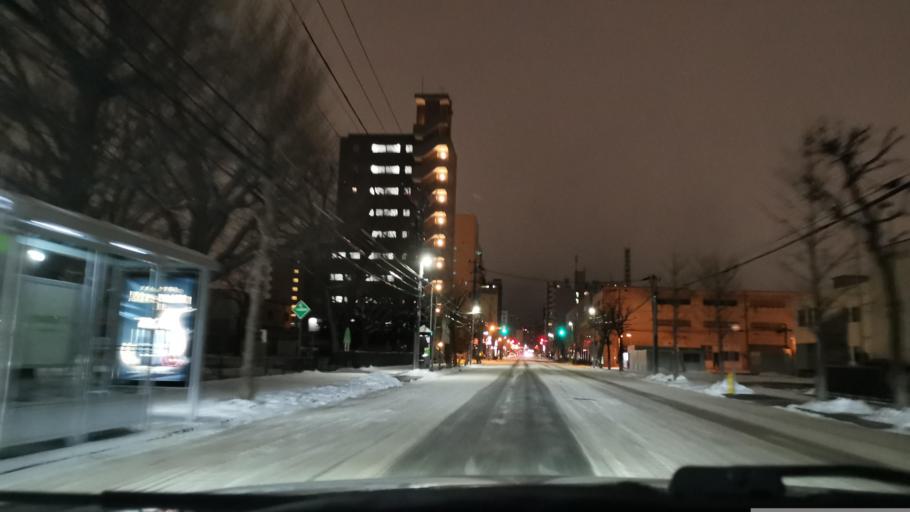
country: JP
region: Hokkaido
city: Sapporo
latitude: 43.0604
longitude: 141.3751
